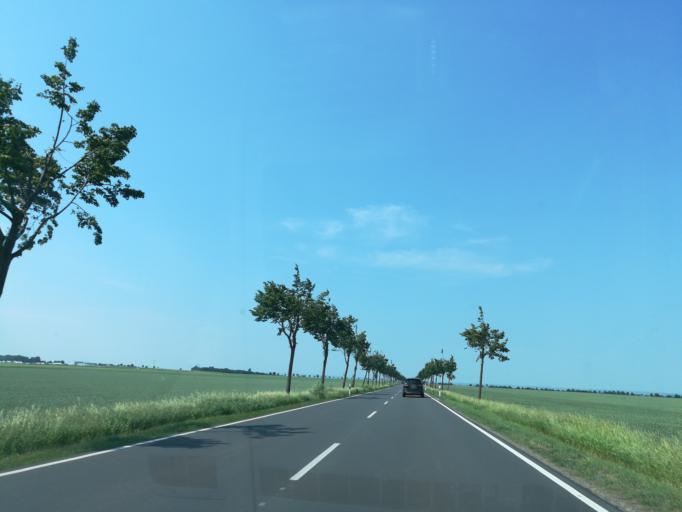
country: DE
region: Saxony-Anhalt
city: Gross Bornecke
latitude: 51.8494
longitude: 11.4535
